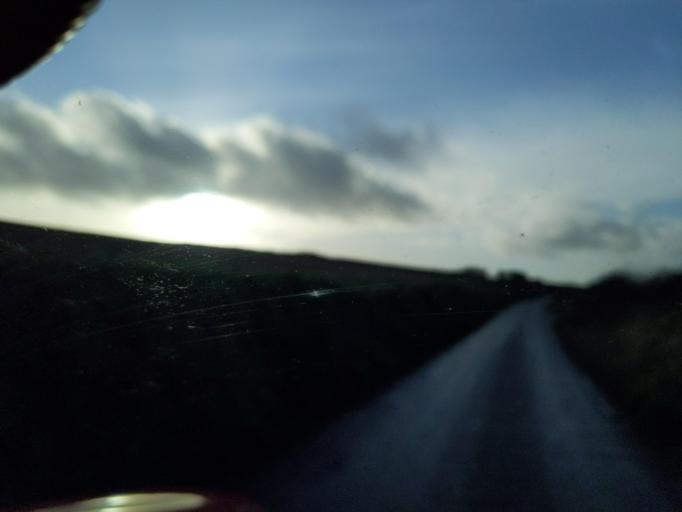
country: GB
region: England
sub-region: Cornwall
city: Fowey
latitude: 50.3325
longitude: -4.6020
